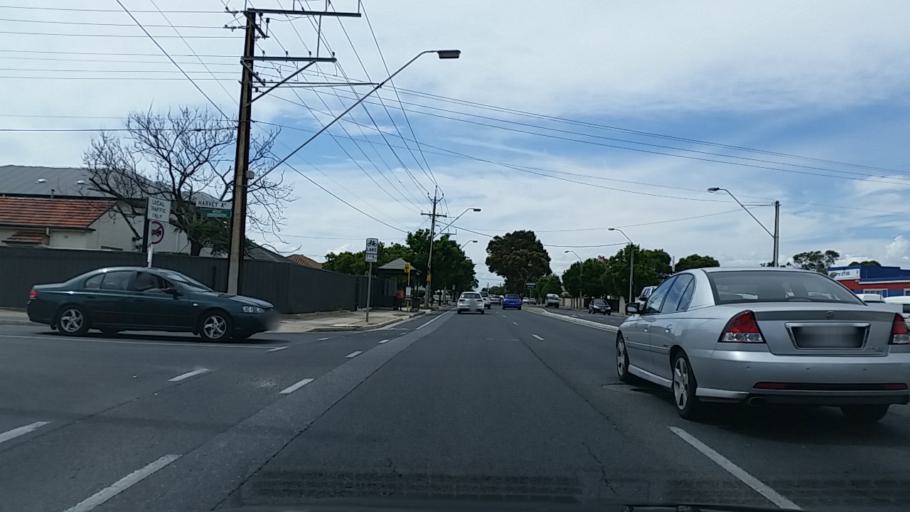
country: AU
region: South Australia
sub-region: City of West Torrens
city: Plympton
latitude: -34.9514
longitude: 138.5538
